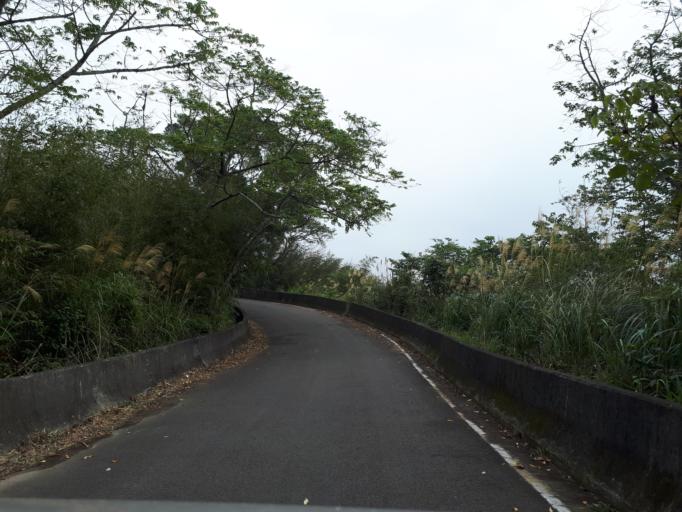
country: TW
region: Taiwan
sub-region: Hsinchu
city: Hsinchu
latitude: 24.7280
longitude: 121.0474
